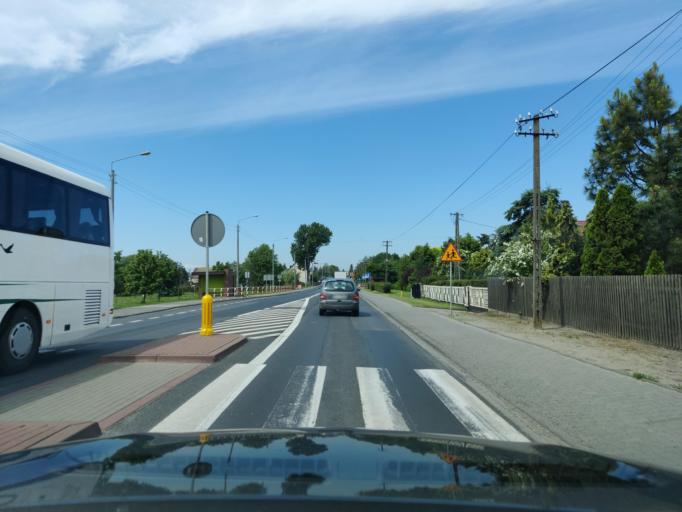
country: PL
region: Greater Poland Voivodeship
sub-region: Powiat grodziski
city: Granowo
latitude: 52.2224
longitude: 16.5329
